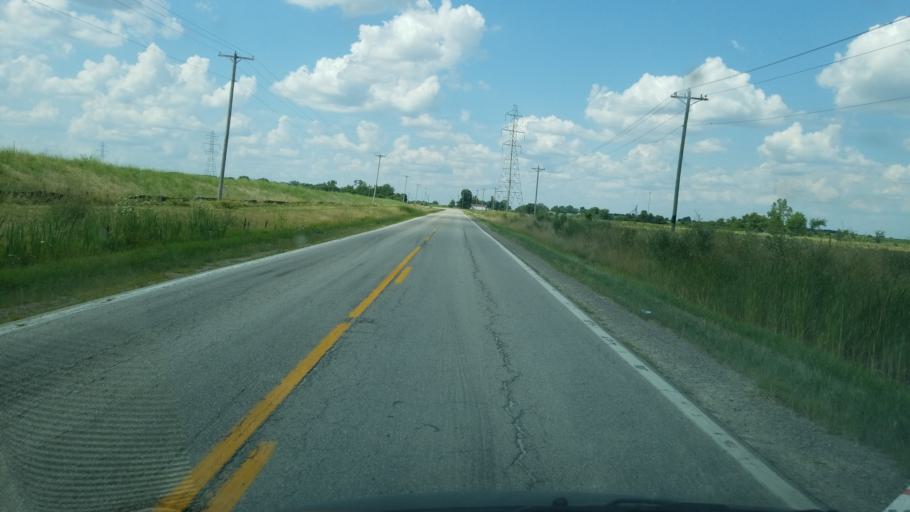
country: US
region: Ohio
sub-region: Union County
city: Richwood
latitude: 40.4182
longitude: -83.4536
